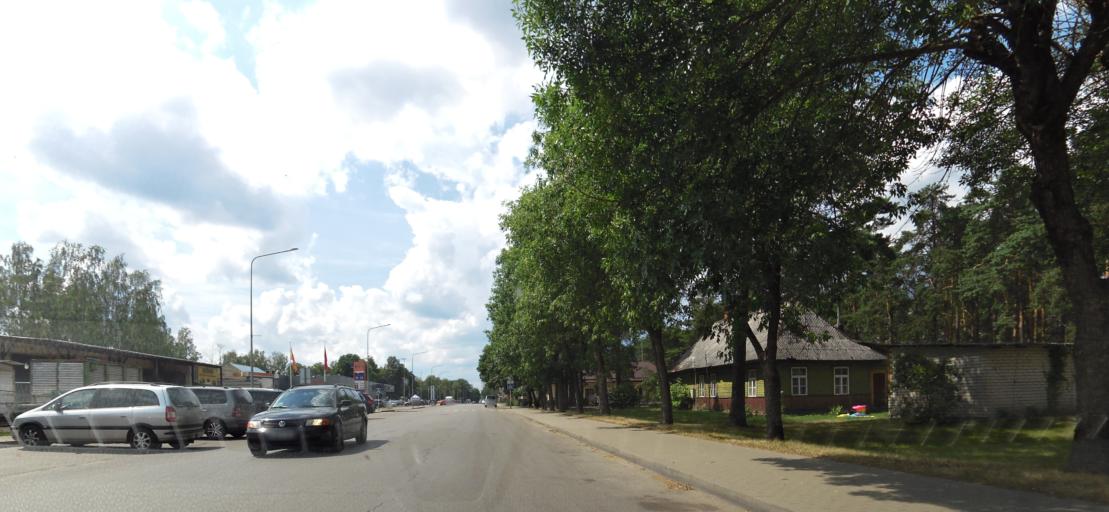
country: LT
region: Alytaus apskritis
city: Varena
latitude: 54.2112
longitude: 24.5790
